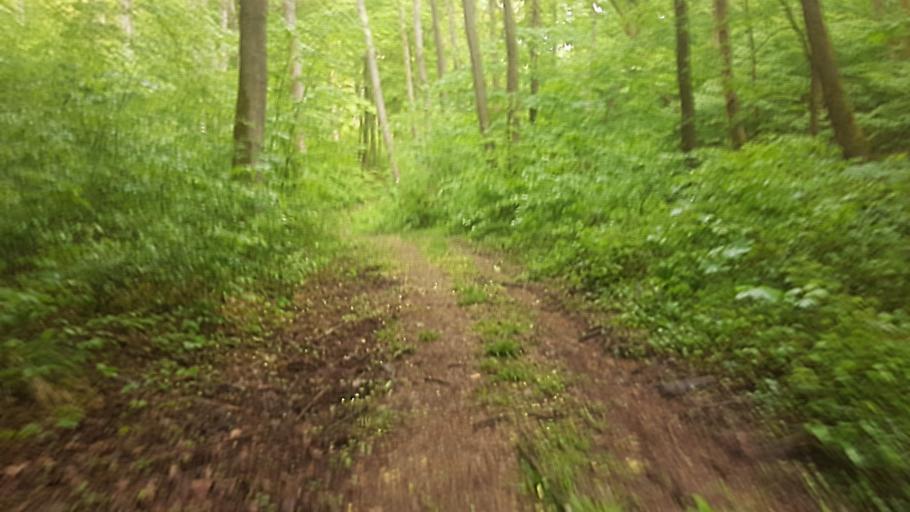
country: FR
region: Champagne-Ardenne
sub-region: Departement des Ardennes
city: Haybes
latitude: 50.0591
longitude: 4.6208
